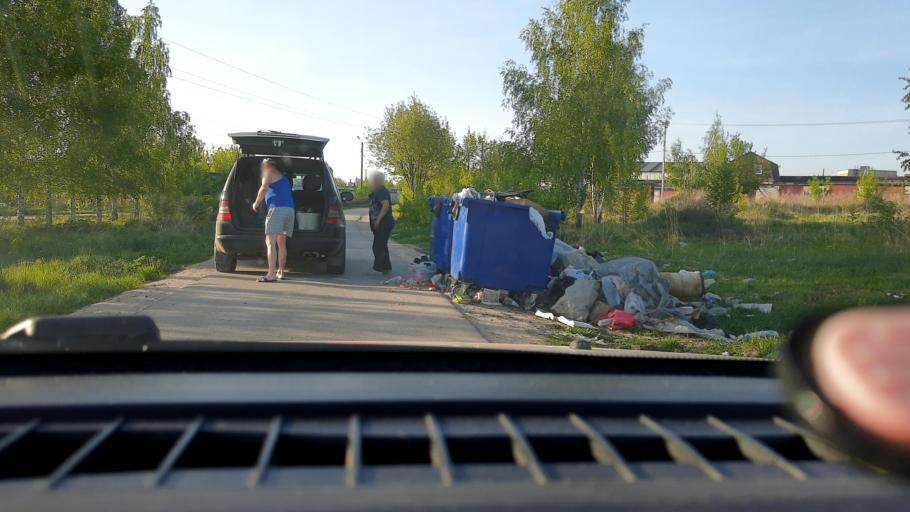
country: RU
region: Nizjnij Novgorod
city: Kstovo
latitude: 56.1328
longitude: 44.1913
